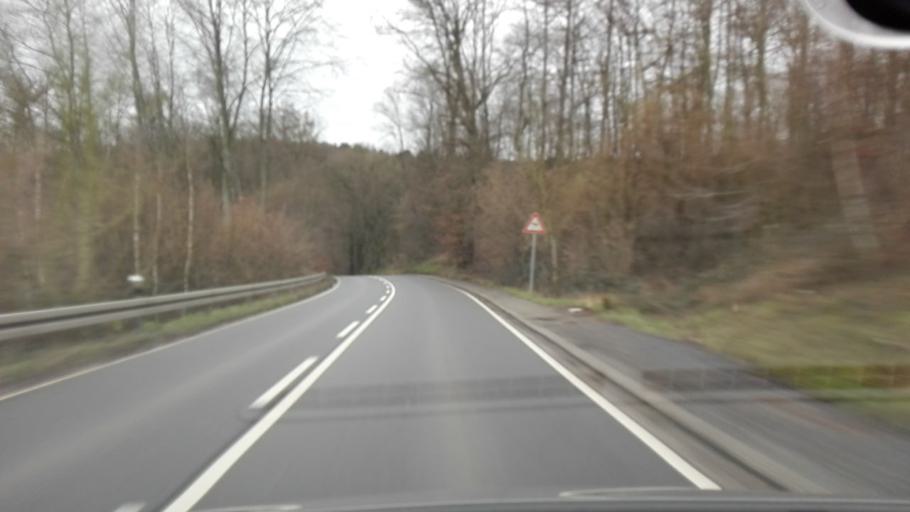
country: DE
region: North Rhine-Westphalia
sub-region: Regierungsbezirk Arnsberg
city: Frondenberg
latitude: 51.4794
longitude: 7.7377
